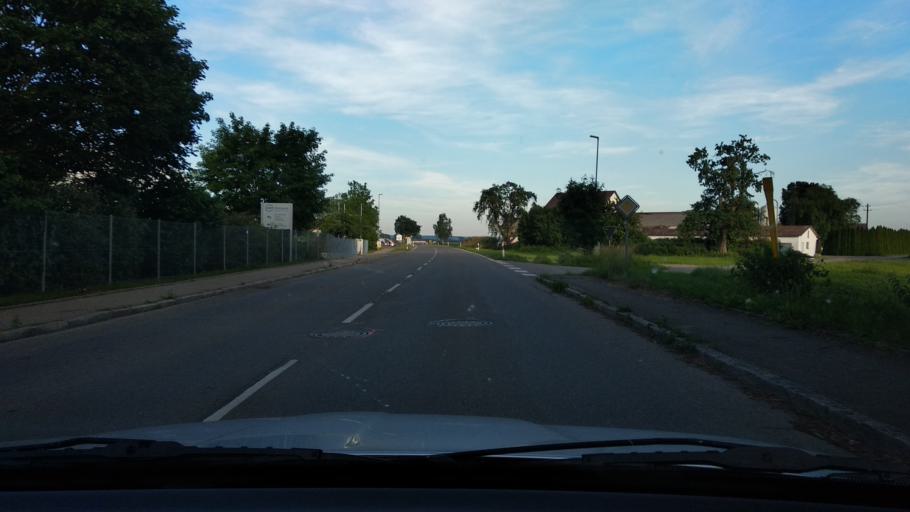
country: DE
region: Baden-Wuerttemberg
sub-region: Tuebingen Region
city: Kirchberg an der Iller
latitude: 48.1299
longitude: 10.0852
